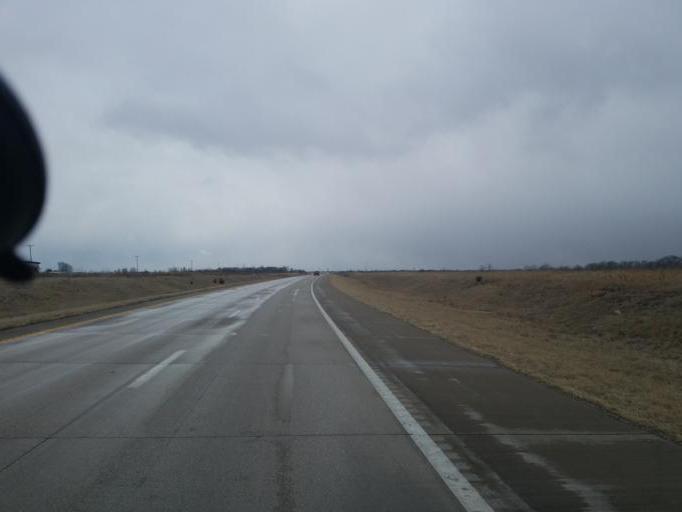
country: US
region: Missouri
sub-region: Randolph County
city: Moberly
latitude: 39.4885
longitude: -92.4345
